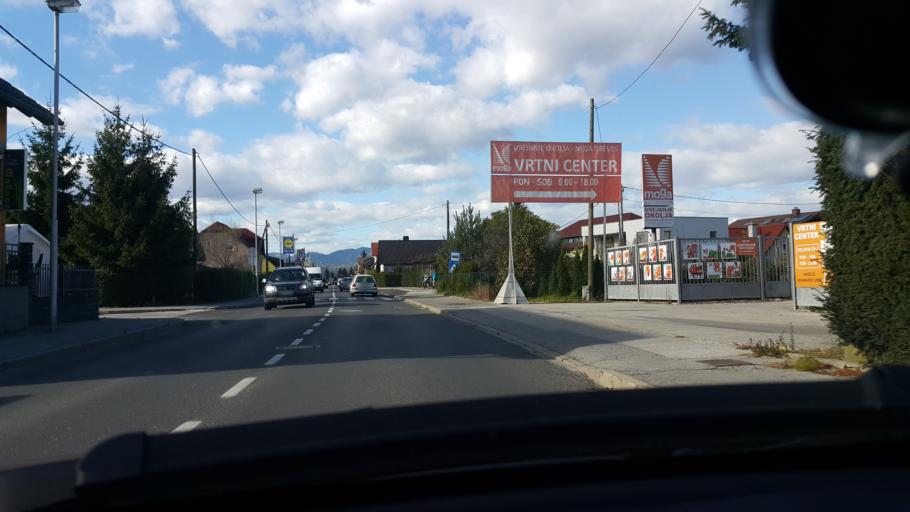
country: SI
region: Maribor
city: Maribor
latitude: 46.5446
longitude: 15.6773
